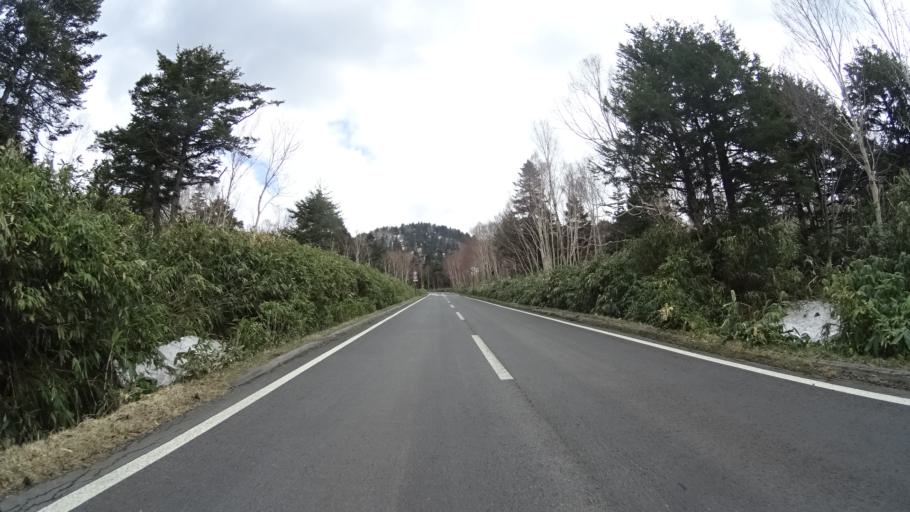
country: JP
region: Nagano
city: Nakano
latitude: 36.6773
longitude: 138.5075
